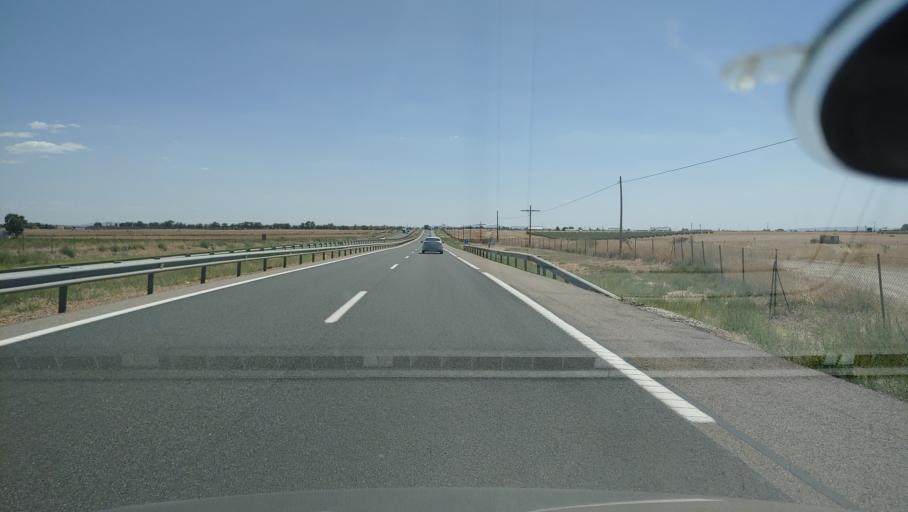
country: ES
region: Castille-La Mancha
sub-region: Provincia de Ciudad Real
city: Villarta de San Juan
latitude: 39.1415
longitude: -3.3836
